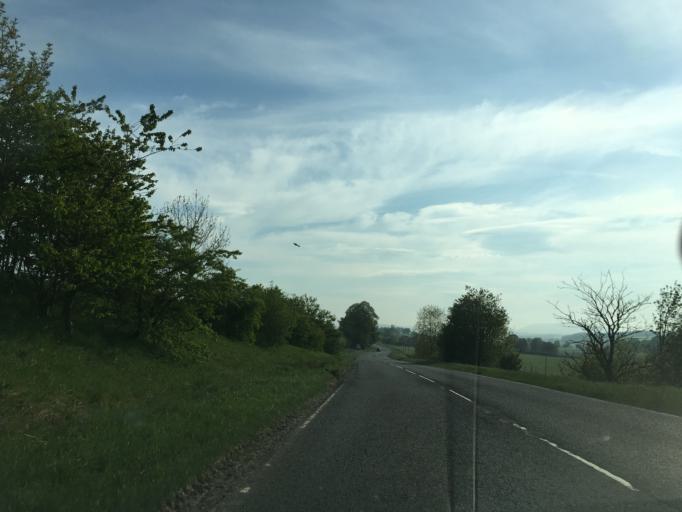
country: GB
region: Scotland
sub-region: The Scottish Borders
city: West Linton
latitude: 55.7516
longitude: -3.2820
